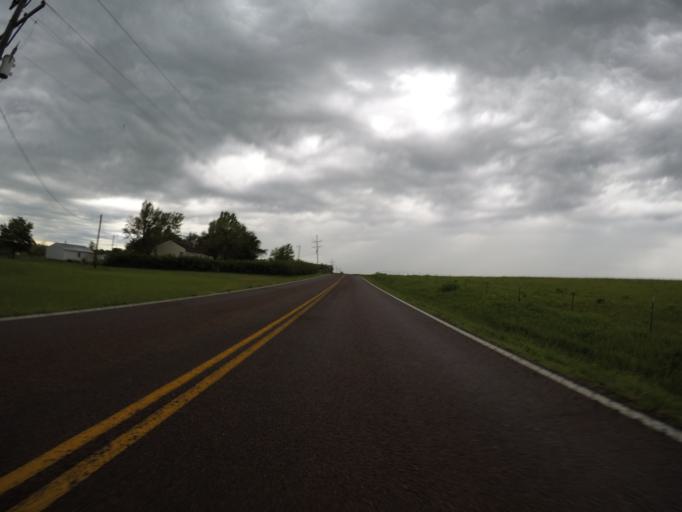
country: US
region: Kansas
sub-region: Shawnee County
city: Rossville
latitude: 38.9574
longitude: -96.0448
